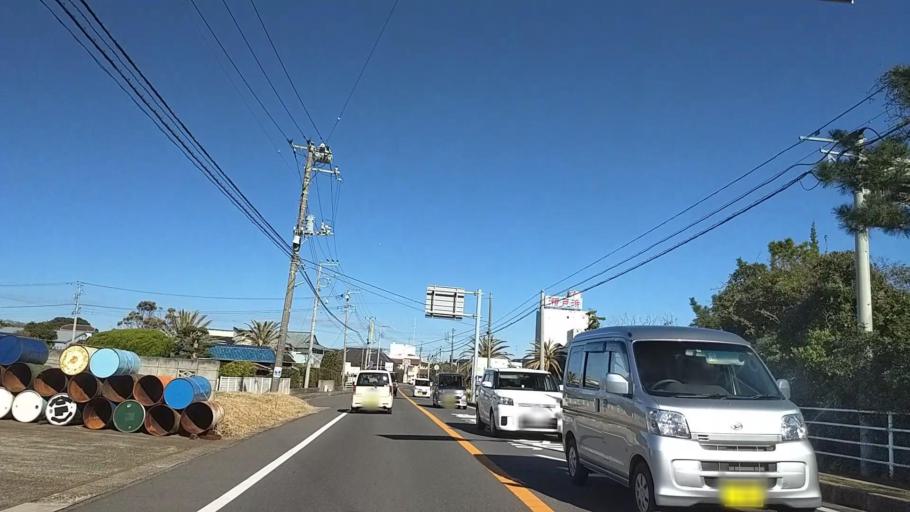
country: JP
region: Chiba
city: Tateyama
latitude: 34.9737
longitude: 139.9624
